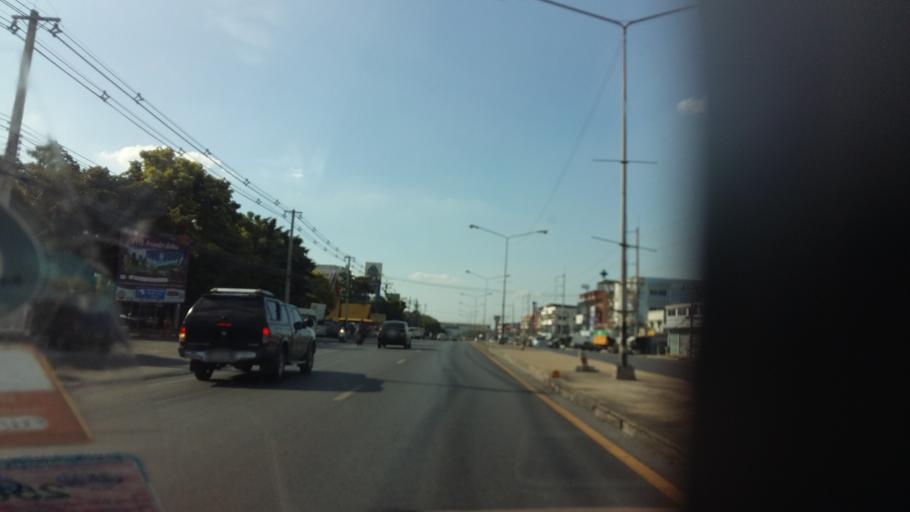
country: TH
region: Lop Buri
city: Lop Buri
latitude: 14.8237
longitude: 100.6477
